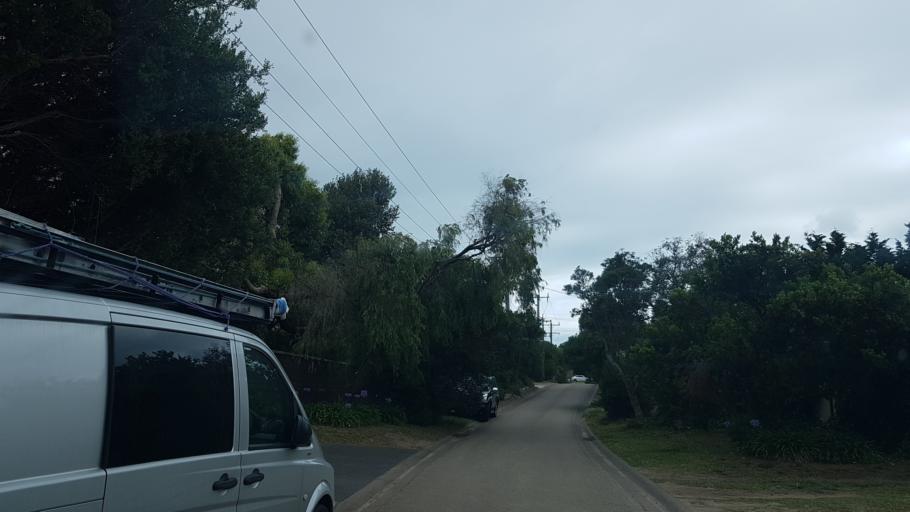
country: AU
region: Victoria
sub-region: Mornington Peninsula
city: Blairgowrie
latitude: -38.3773
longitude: 144.7791
